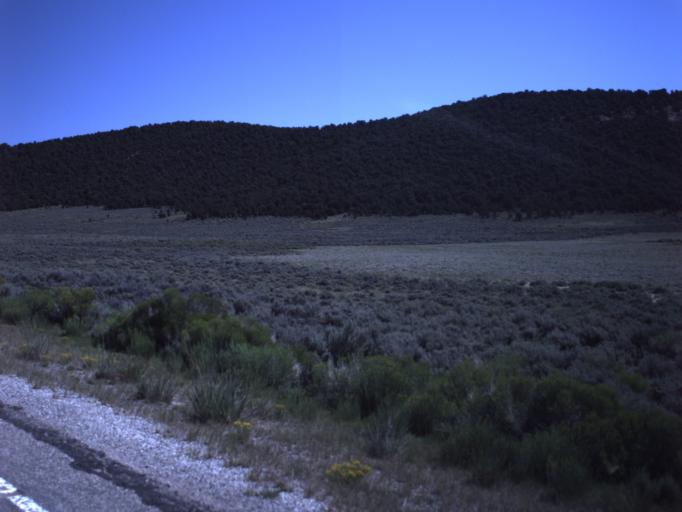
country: US
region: Utah
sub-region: Wayne County
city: Loa
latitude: 38.6400
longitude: -111.4335
